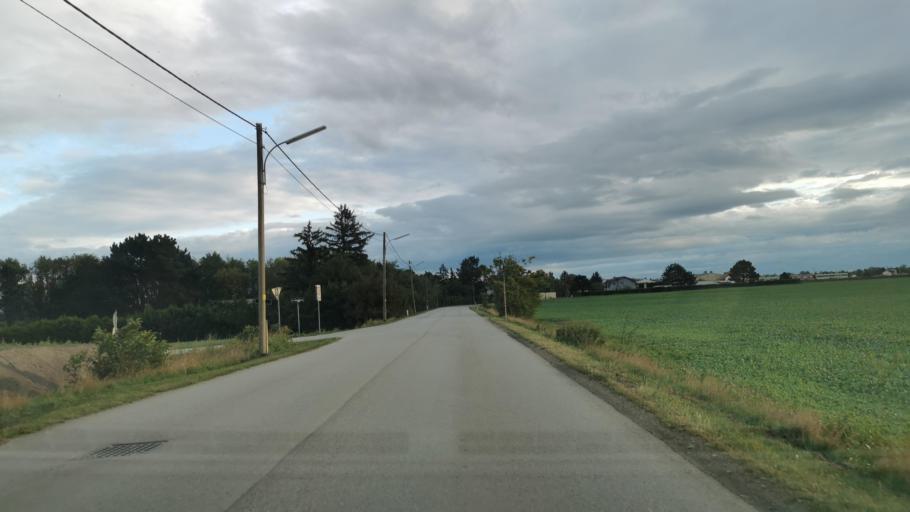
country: AT
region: Lower Austria
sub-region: Politischer Bezirk Ganserndorf
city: Aderklaa
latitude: 48.2453
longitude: 16.4944
